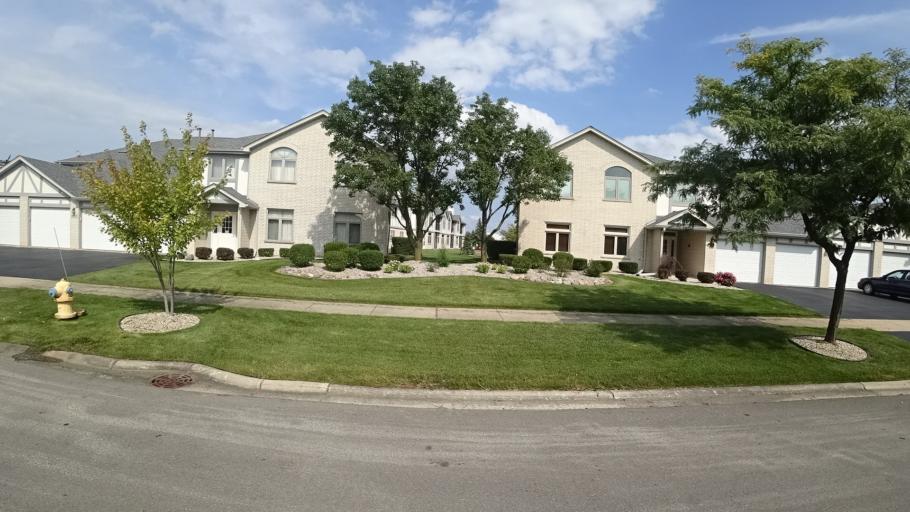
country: US
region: Illinois
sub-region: Cook County
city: Tinley Park
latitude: 41.5574
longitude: -87.7752
